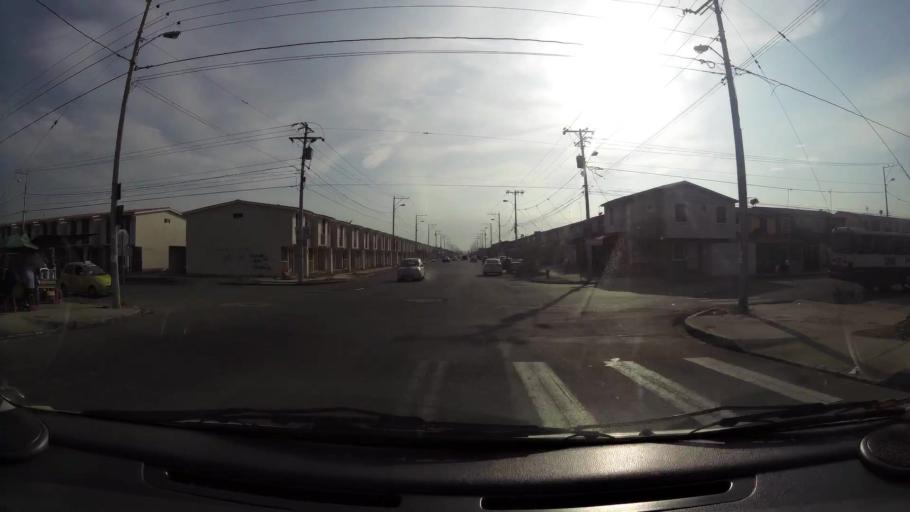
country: EC
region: Guayas
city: Eloy Alfaro
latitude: -2.0686
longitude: -79.8985
